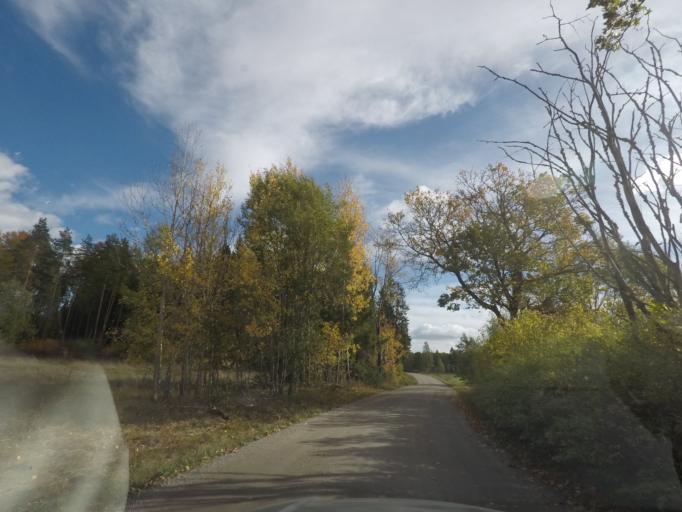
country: SE
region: Soedermanland
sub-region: Eskilstuna Kommun
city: Kvicksund
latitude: 59.3243
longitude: 16.2379
